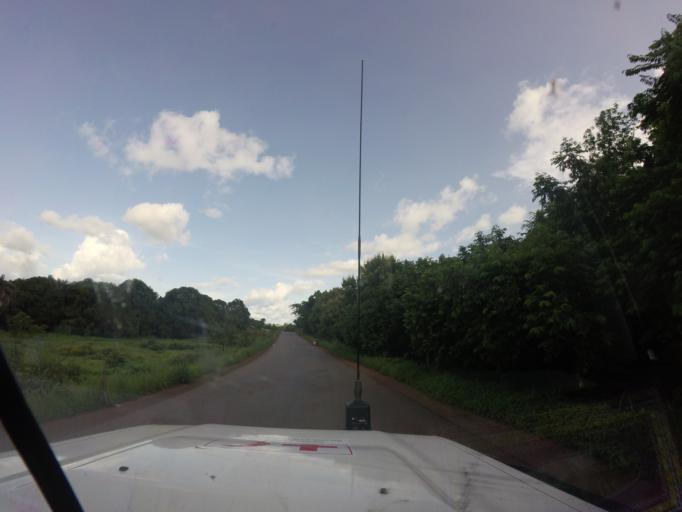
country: GN
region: Mamou
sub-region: Mamou Prefecture
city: Mamou
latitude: 10.1997
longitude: -12.4667
